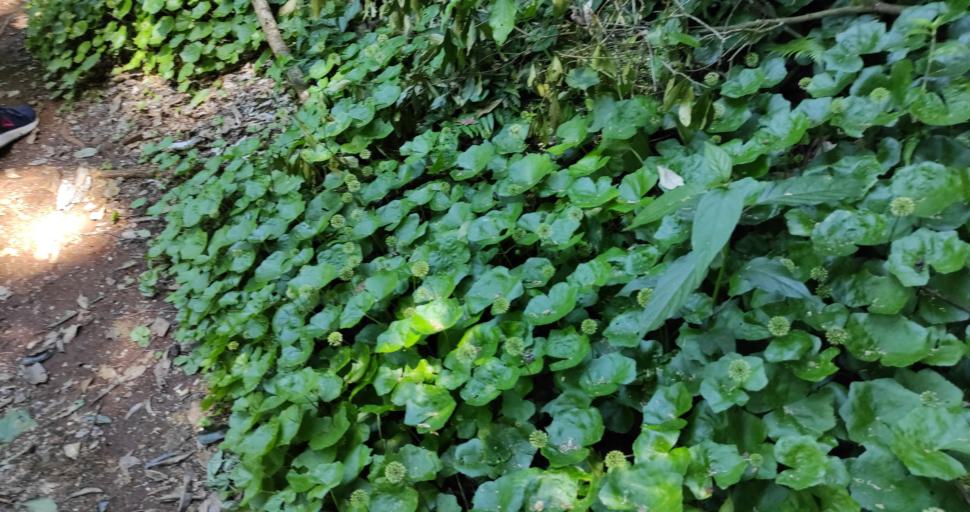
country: BR
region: Rio Grande do Sul
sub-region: Tres Passos
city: Tres Passos
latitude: -27.1476
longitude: -53.8973
